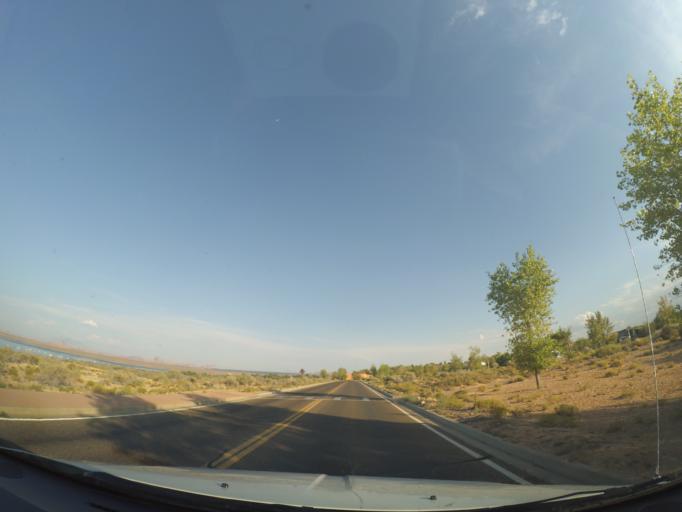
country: US
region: Arizona
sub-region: Coconino County
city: Page
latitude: 37.0007
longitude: -111.5002
